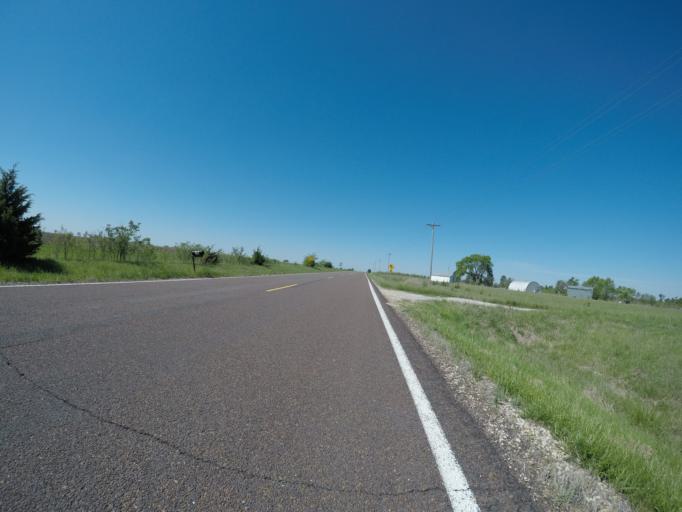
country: US
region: Kansas
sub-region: Osage County
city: Overbrook
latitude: 38.8678
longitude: -95.4603
